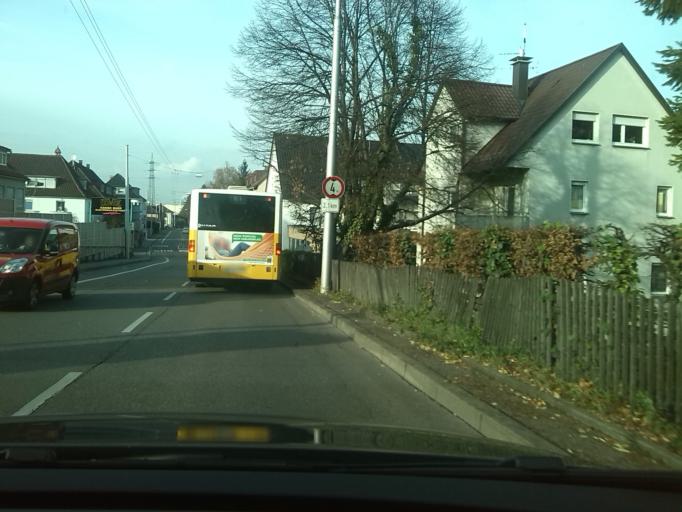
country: DE
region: Baden-Wuerttemberg
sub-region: Regierungsbezirk Stuttgart
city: Ostfildern
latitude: 48.7649
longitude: 9.2667
